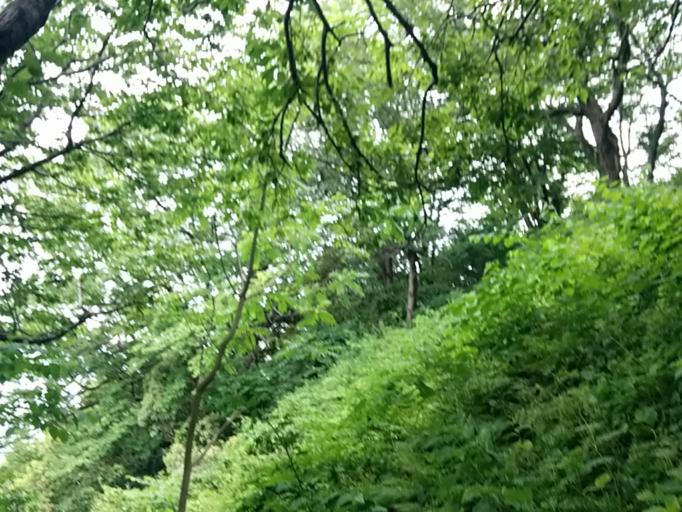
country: JP
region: Kyoto
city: Miyazu
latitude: 35.7758
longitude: 135.2231
